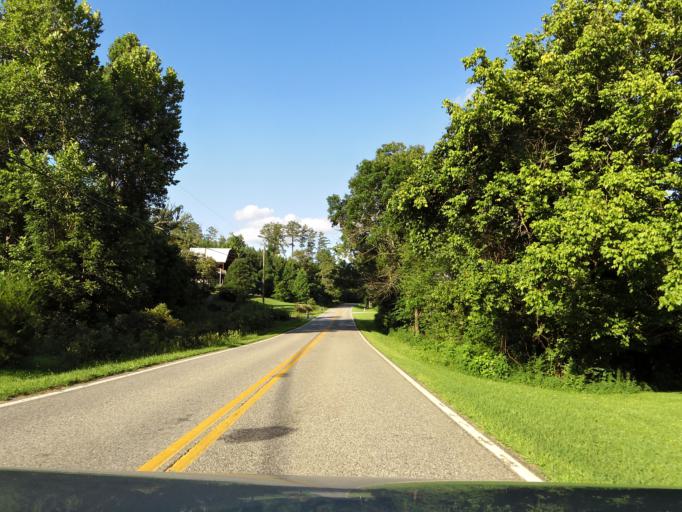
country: US
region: Tennessee
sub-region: Blount County
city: Maryville
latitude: 35.6478
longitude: -83.9849
